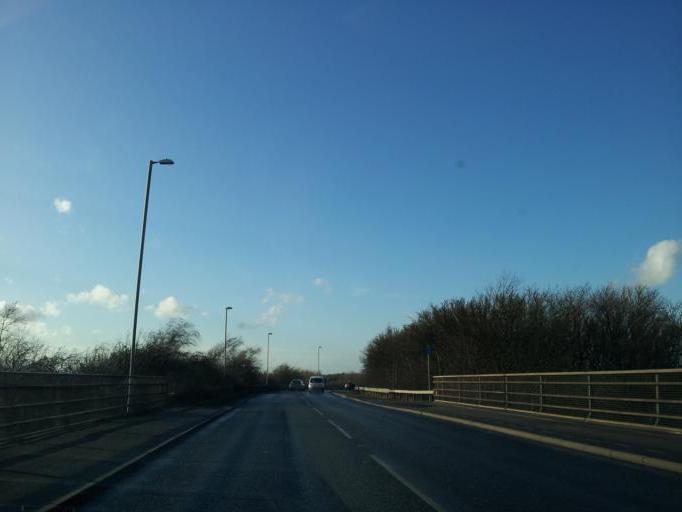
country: GB
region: England
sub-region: Nottinghamshire
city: Newark on Trent
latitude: 53.0465
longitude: -0.7780
